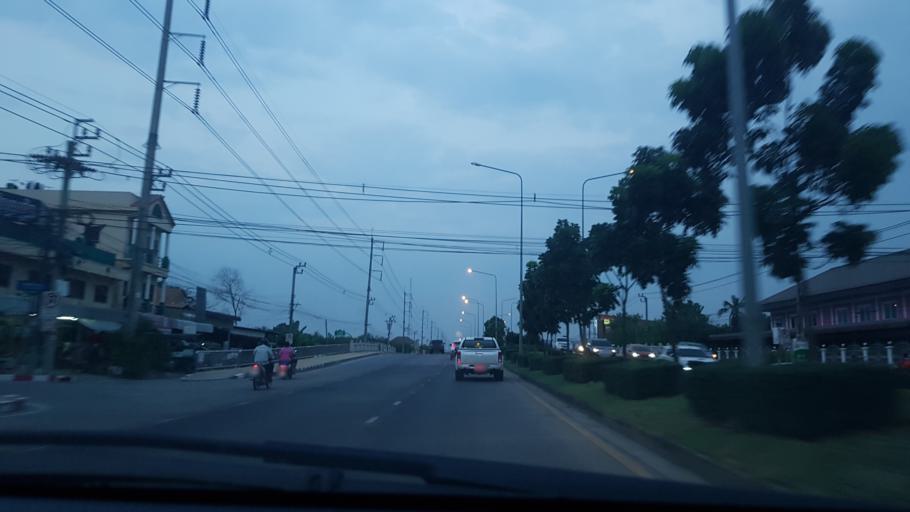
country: TH
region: Bangkok
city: Nong Khaem
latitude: 13.7374
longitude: 100.3638
